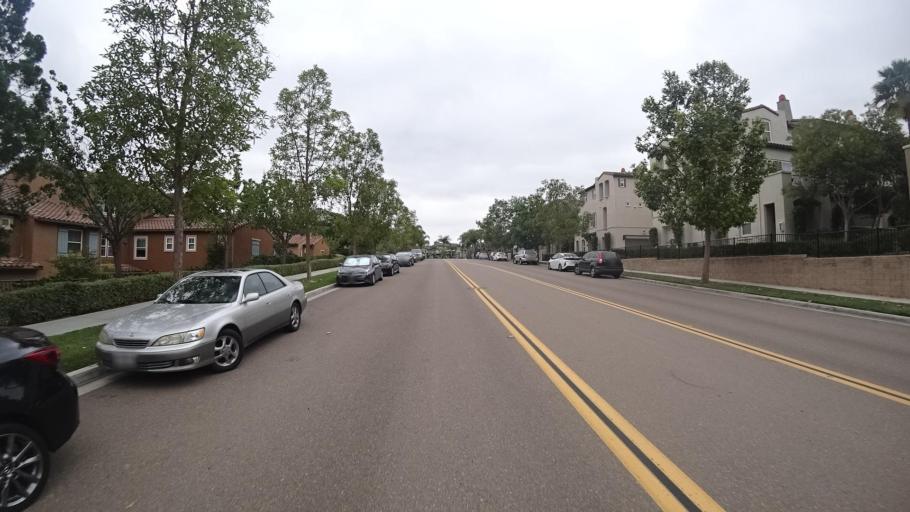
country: US
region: California
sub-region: San Diego County
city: Fairbanks Ranch
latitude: 33.0229
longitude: -117.1113
